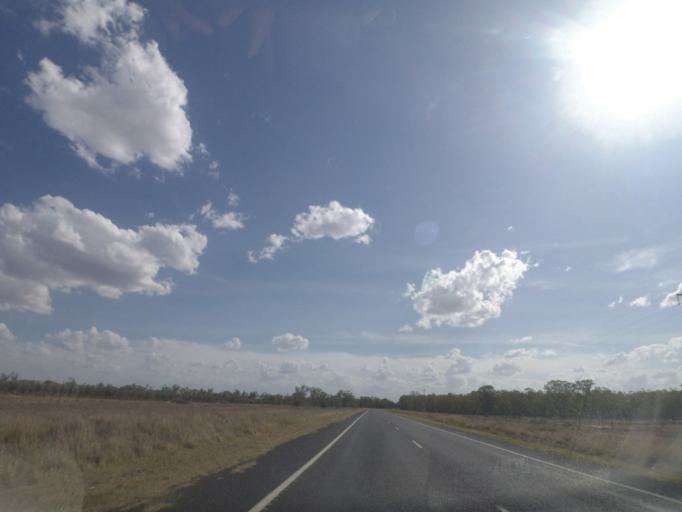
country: AU
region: New South Wales
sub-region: Moree Plains
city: Boggabilla
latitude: -28.5336
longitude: 150.8943
